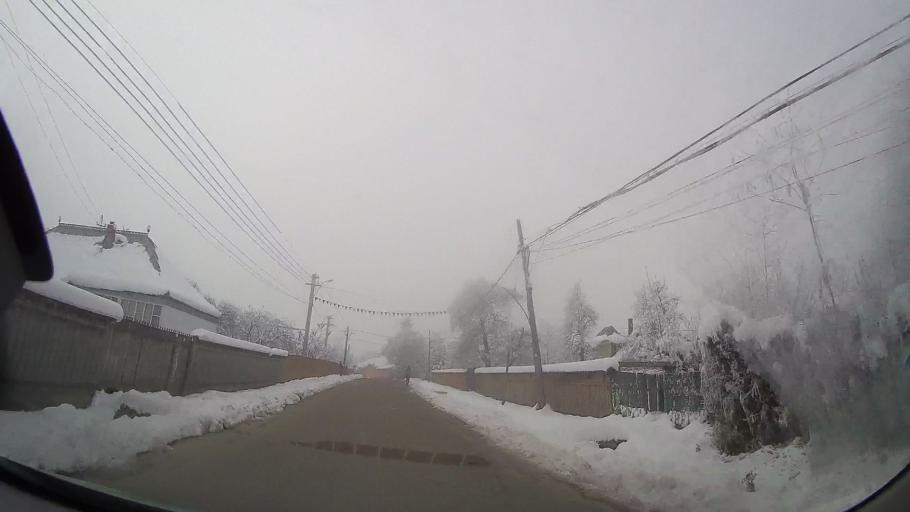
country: RO
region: Iasi
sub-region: Comuna Valea Seaca
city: Valea Seaca
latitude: 47.2925
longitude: 26.6680
